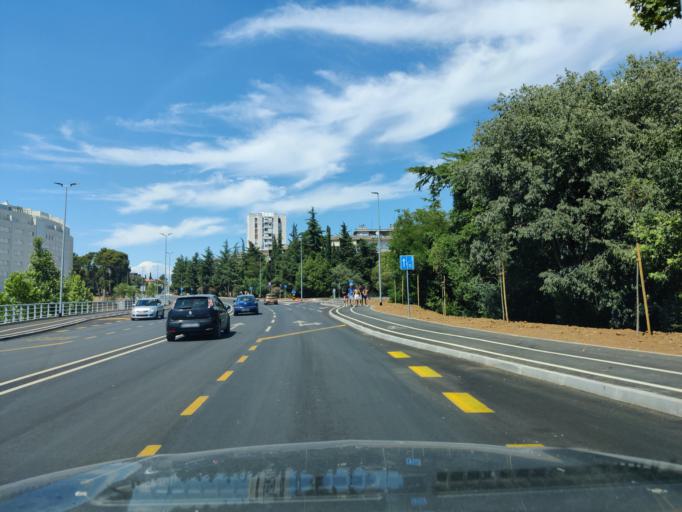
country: HR
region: Zadarska
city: Zadar
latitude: 44.1142
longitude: 15.2362
